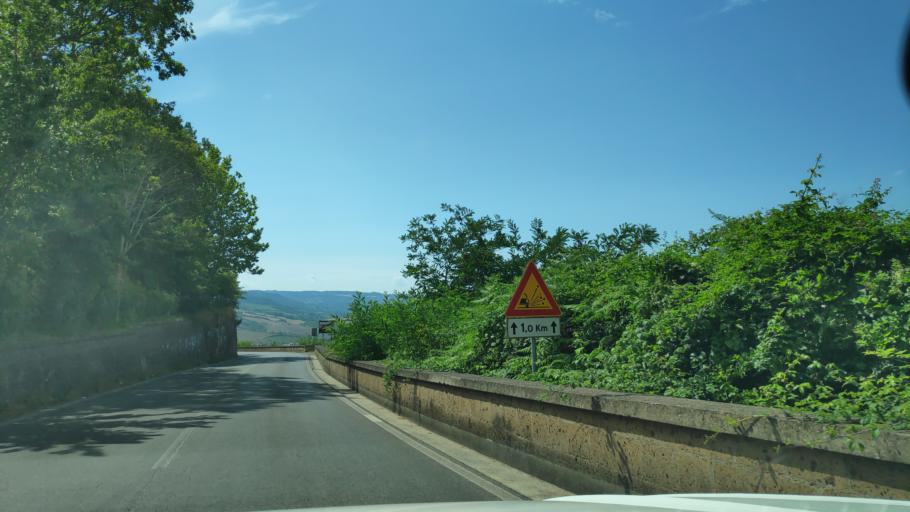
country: IT
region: Umbria
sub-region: Provincia di Terni
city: Orvieto
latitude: 42.7236
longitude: 12.1174
